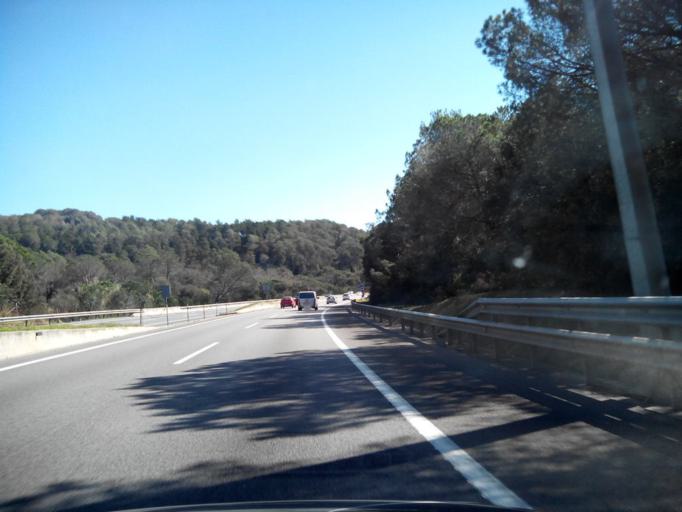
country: ES
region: Catalonia
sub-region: Provincia de Barcelona
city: Argentona
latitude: 41.5791
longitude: 2.3799
